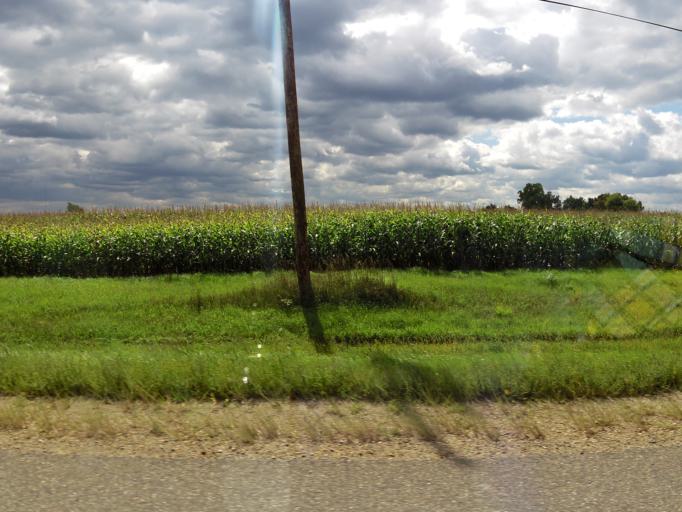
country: US
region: Minnesota
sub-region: Dakota County
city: Rosemount
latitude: 44.7174
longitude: -93.0948
